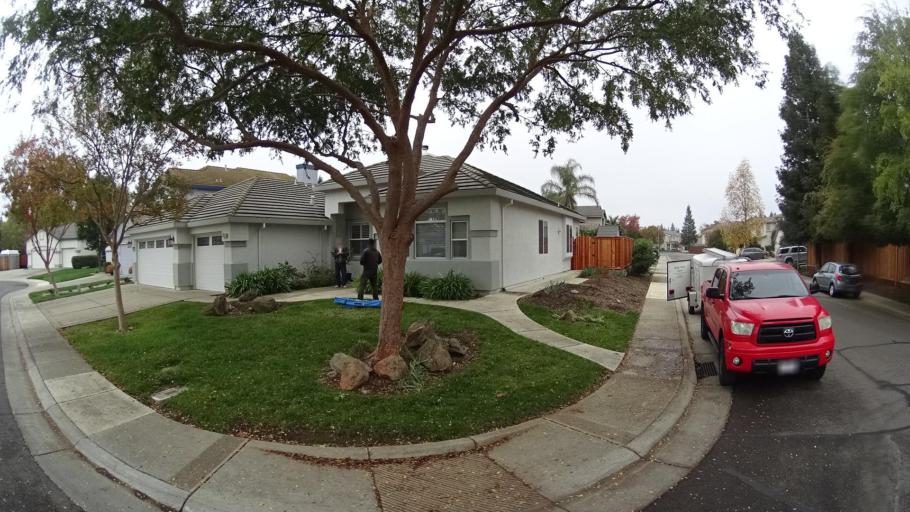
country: US
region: California
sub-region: Sacramento County
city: Elk Grove
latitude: 38.4101
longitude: -121.3434
